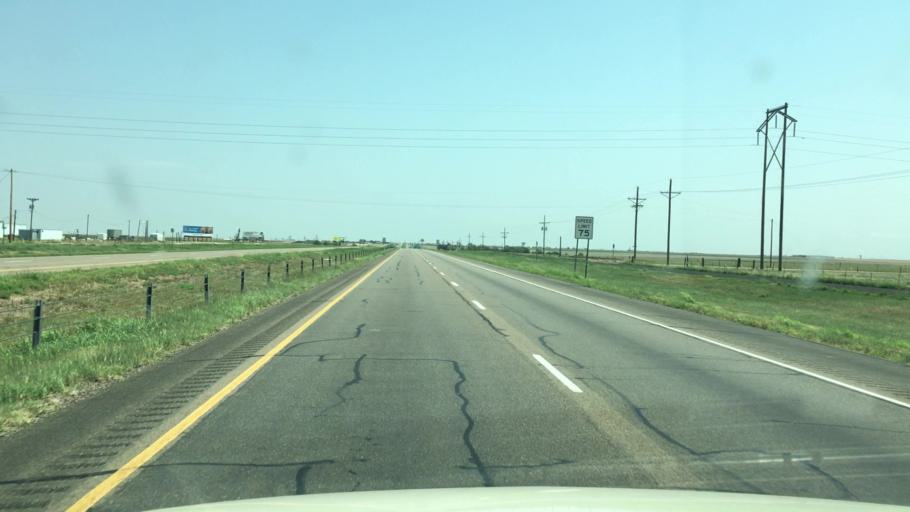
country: US
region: Texas
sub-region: Potter County
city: Bushland
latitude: 35.1909
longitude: -102.0477
